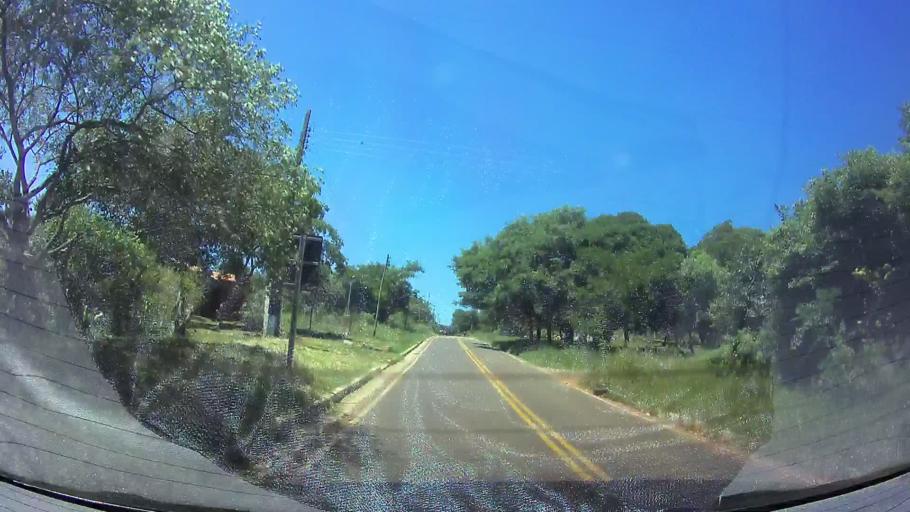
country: PY
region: Central
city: Aregua
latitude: -25.2418
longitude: -57.4360
